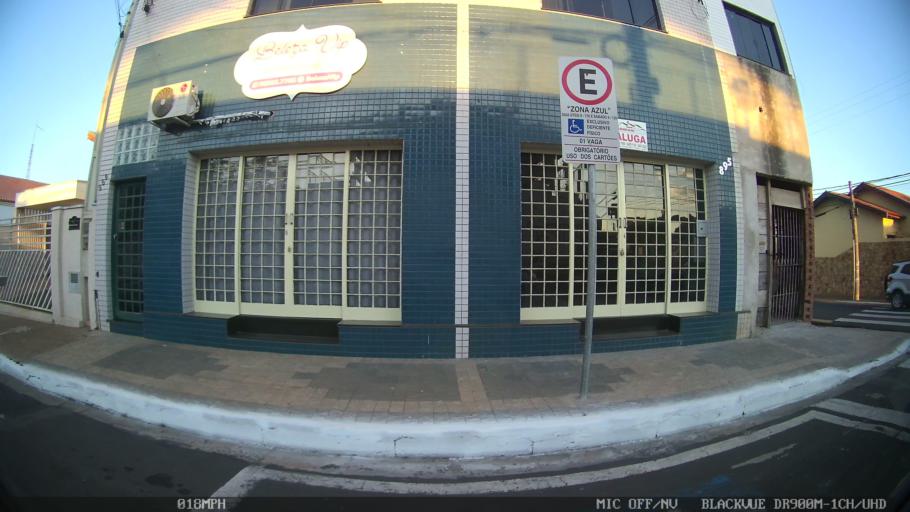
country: BR
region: Sao Paulo
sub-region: Santa Barbara D'Oeste
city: Santa Barbara d'Oeste
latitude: -22.7564
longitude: -47.4167
